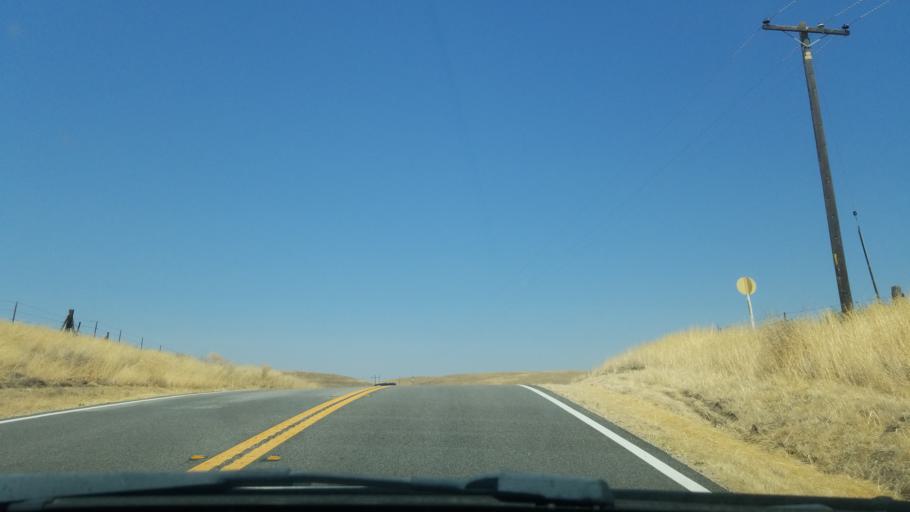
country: US
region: California
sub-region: San Luis Obispo County
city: Shandon
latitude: 35.5942
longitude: -120.4182
